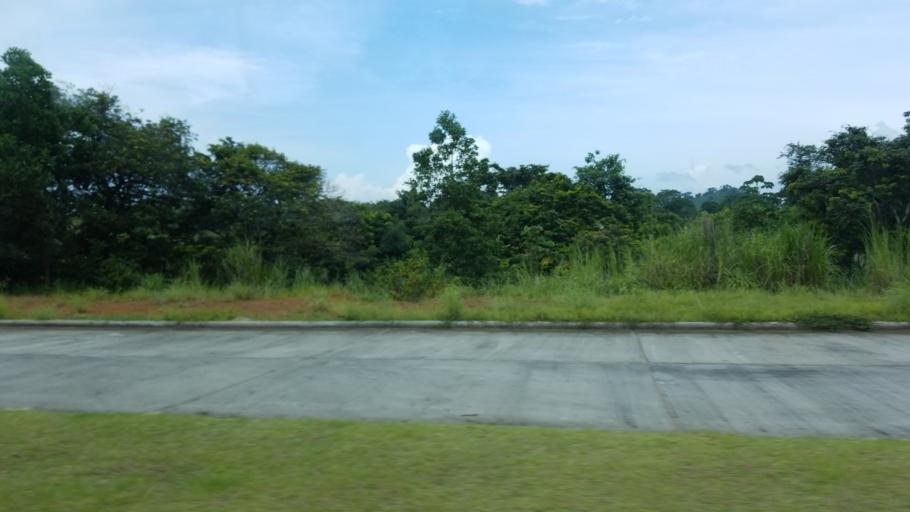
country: PA
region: Panama
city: Las Cumbres
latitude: 9.1096
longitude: -79.4759
